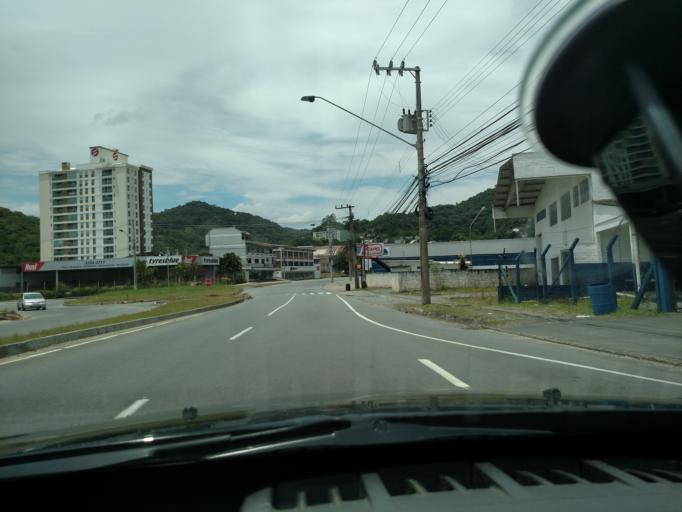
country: BR
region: Santa Catarina
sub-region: Blumenau
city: Blumenau
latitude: -26.8936
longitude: -49.0642
